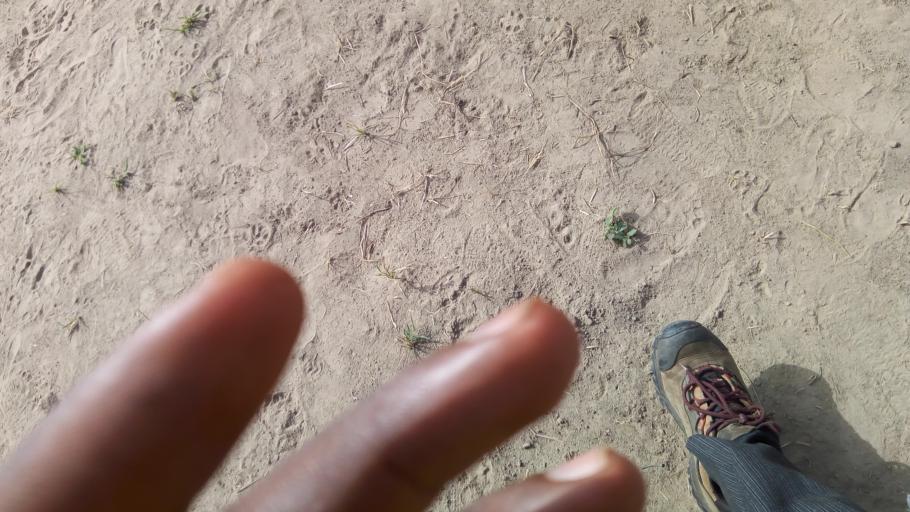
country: ML
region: Kayes
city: Kita
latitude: 13.1973
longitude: -8.7932
